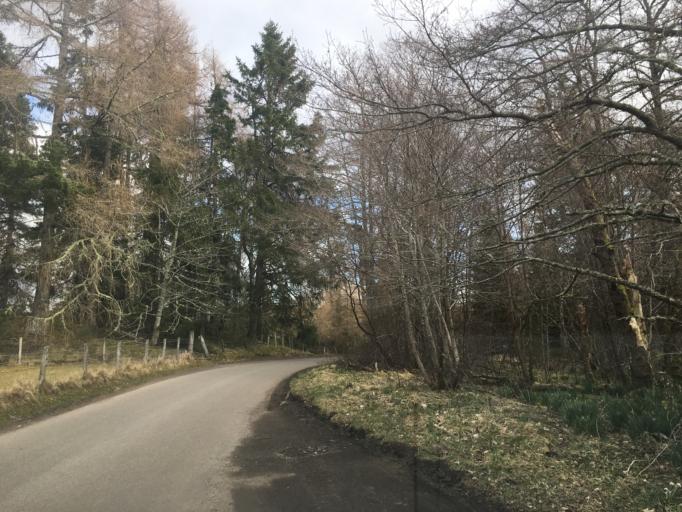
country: GB
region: Scotland
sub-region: Highland
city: Aviemore
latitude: 57.1612
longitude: -3.8292
